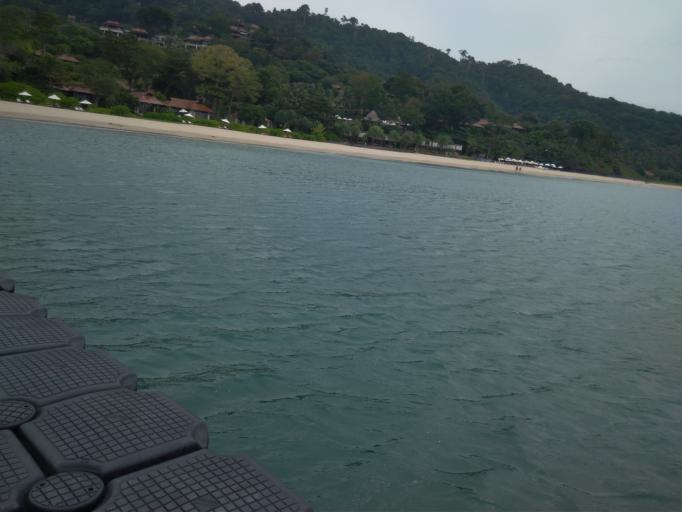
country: TH
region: Krabi
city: Ko Lanta
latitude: 7.4960
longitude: 99.0734
